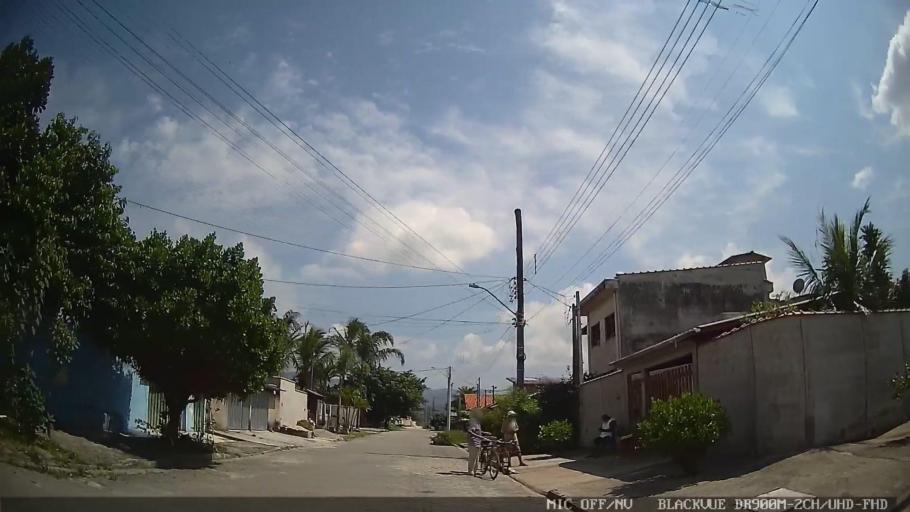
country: BR
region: Sao Paulo
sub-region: Caraguatatuba
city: Caraguatatuba
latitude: -23.6733
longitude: -45.4510
